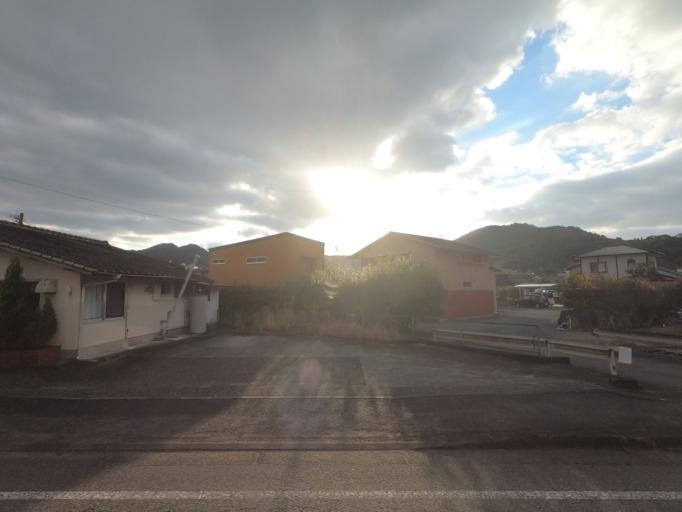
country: JP
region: Kumamoto
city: Minamata
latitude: 32.2705
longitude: 130.5028
